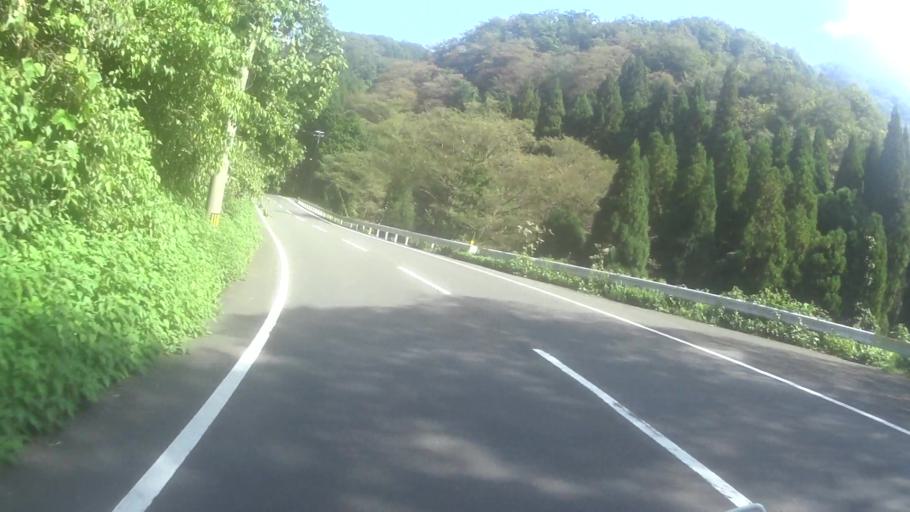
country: JP
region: Kyoto
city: Miyazu
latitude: 35.6400
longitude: 135.1294
